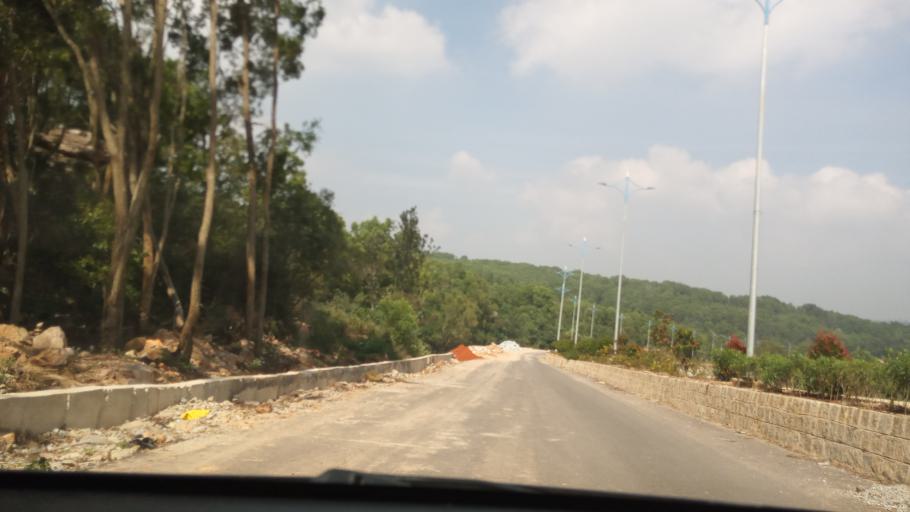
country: IN
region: Andhra Pradesh
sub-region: Chittoor
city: Tirumala
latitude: 13.6877
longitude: 79.3428
